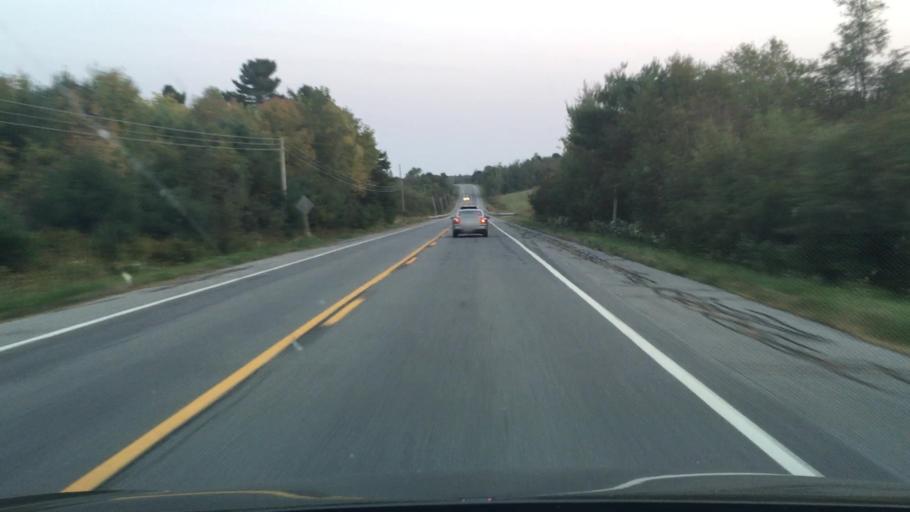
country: US
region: Maine
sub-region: Waldo County
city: Stockton Springs
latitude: 44.5313
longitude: -68.8613
